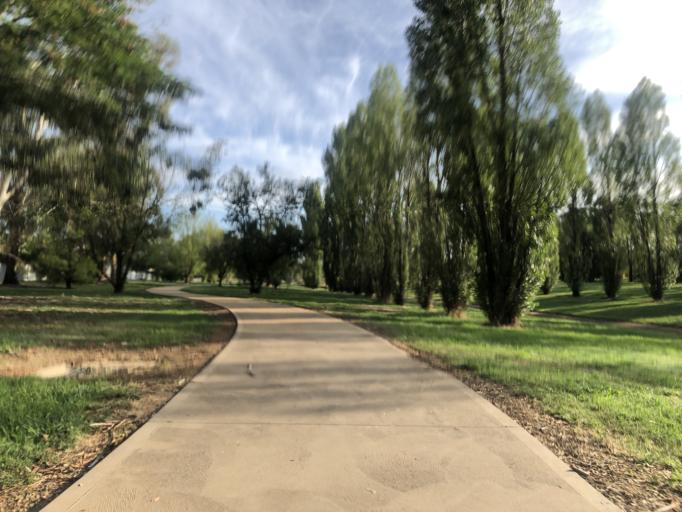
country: AU
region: New South Wales
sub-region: Orange Municipality
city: Orange
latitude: -33.2975
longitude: 149.0916
